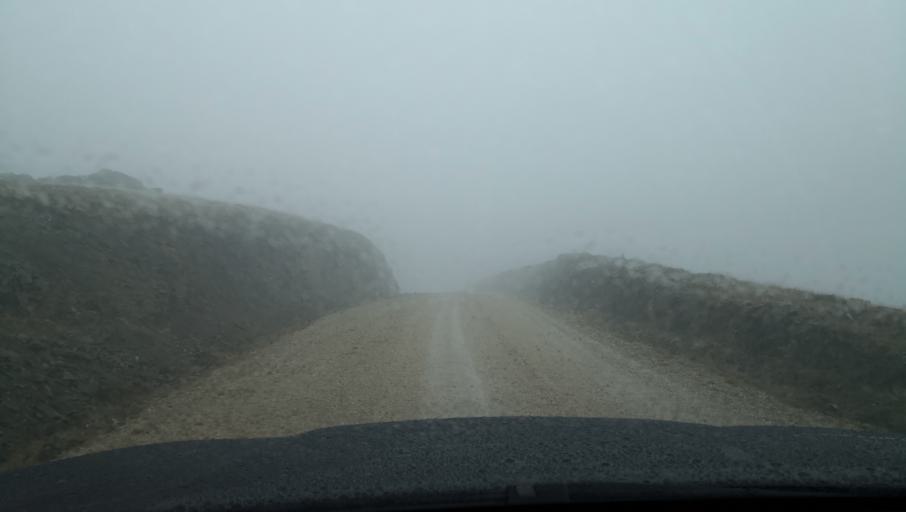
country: PT
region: Vila Real
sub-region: Mondim de Basto
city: Mondim de Basto
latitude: 41.3206
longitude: -7.8823
